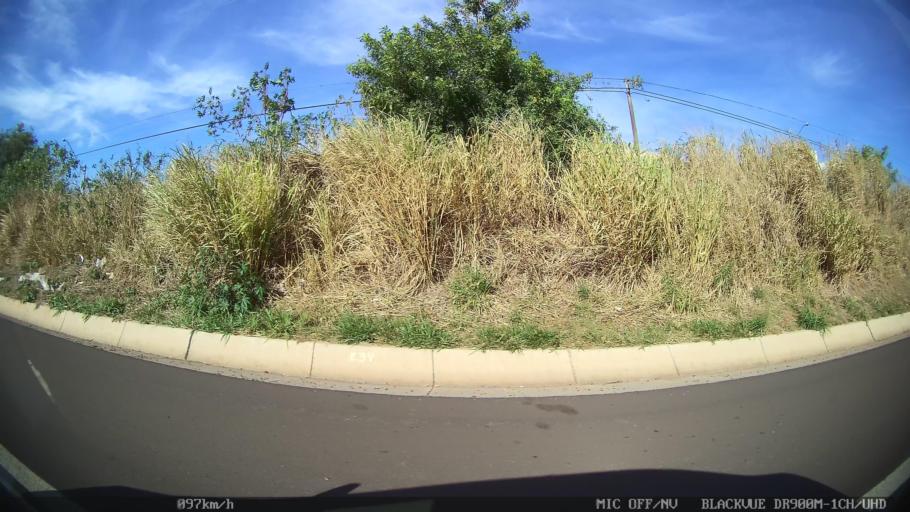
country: BR
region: Sao Paulo
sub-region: Sao Jose Do Rio Preto
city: Sao Jose do Rio Preto
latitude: -20.7551
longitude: -49.3432
